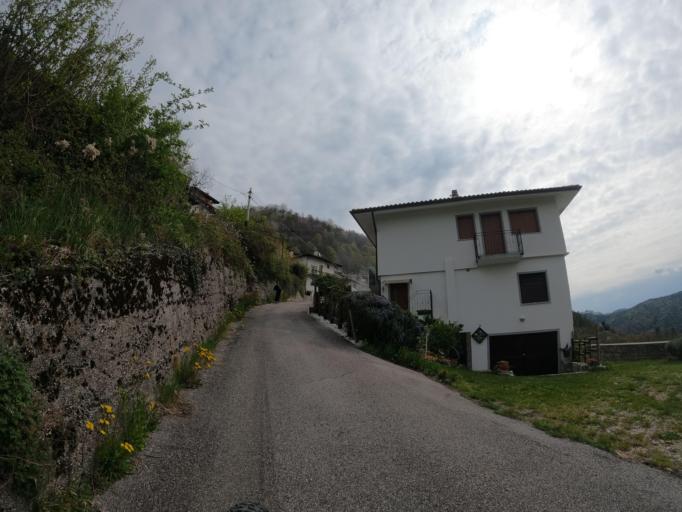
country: IT
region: Friuli Venezia Giulia
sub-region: Provincia di Udine
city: Stregna
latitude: 46.1368
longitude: 13.5908
